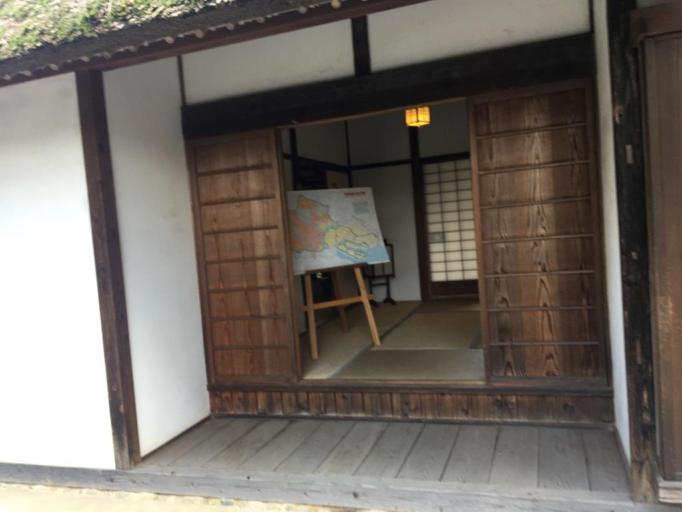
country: JP
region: Gunma
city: Tatebayashi
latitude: 36.2464
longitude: 139.5382
